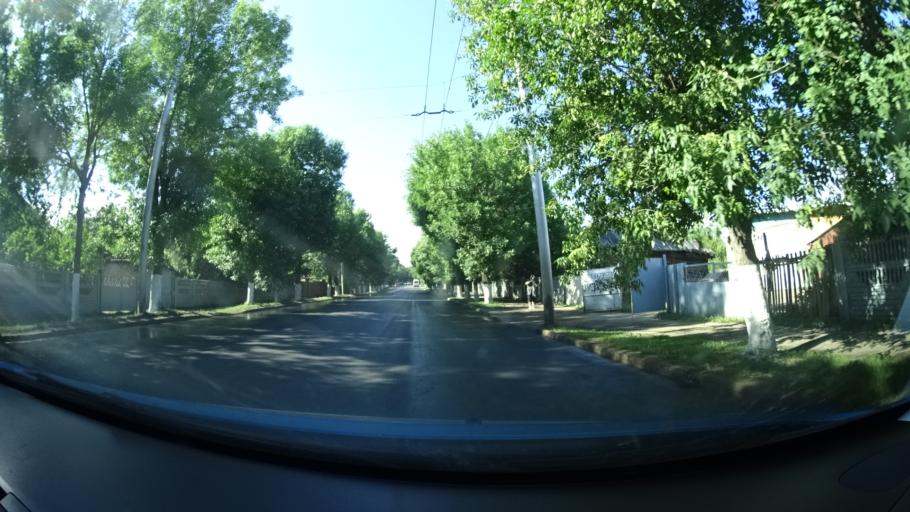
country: RU
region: Bashkortostan
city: Ufa
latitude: 54.8284
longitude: 56.0651
